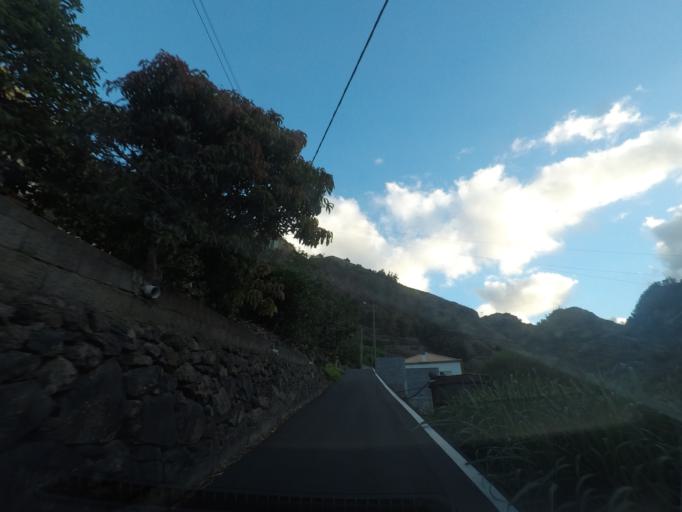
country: PT
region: Madeira
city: Ponta do Sol
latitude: 32.6899
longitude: -17.0747
